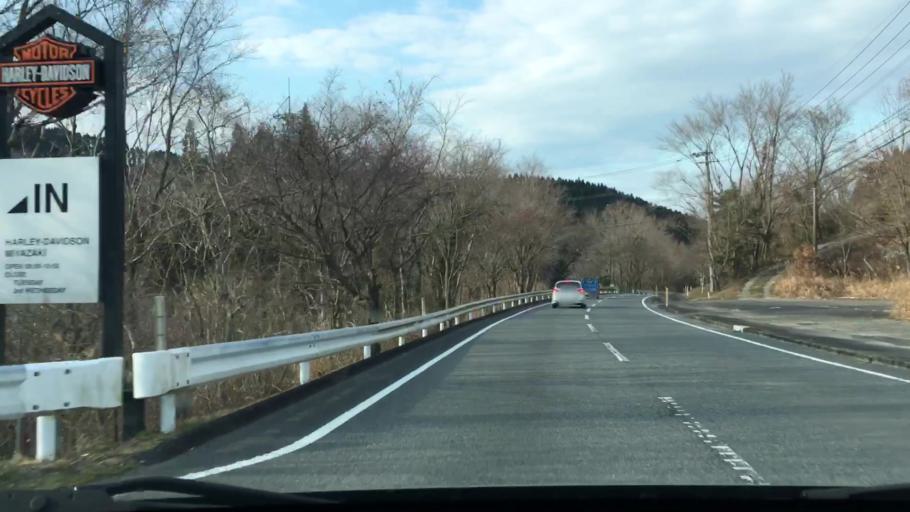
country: JP
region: Miyazaki
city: Miyazaki-shi
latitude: 31.8015
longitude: 131.3022
